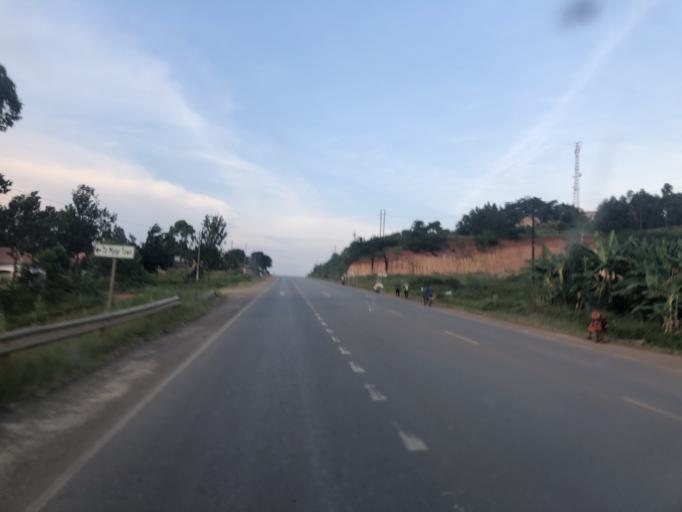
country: UG
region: Central Region
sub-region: Mpigi District
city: Mpigi
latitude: 0.2160
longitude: 32.3284
